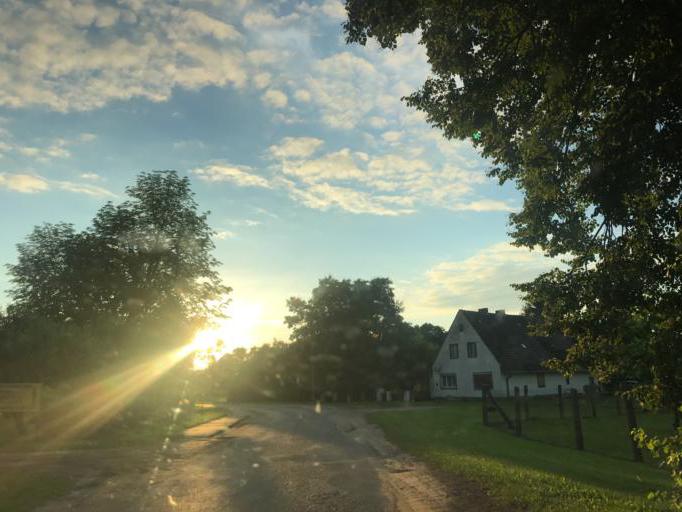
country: DE
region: Mecklenburg-Vorpommern
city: Rechlin
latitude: 53.3383
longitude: 12.8457
